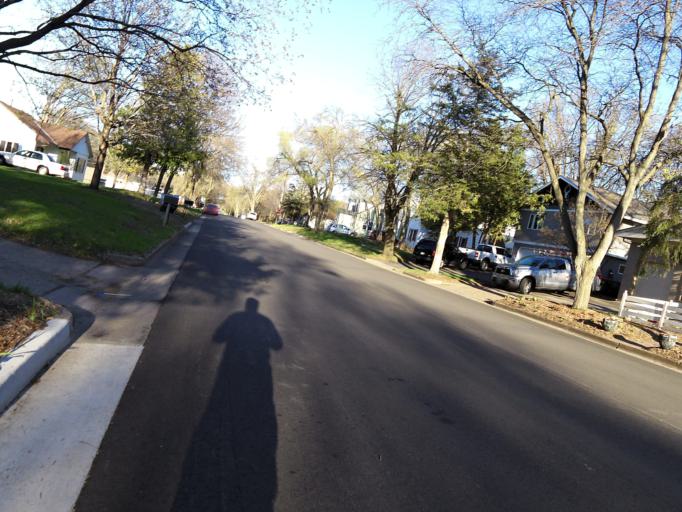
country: US
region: Wisconsin
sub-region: Saint Croix County
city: Hudson
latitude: 44.9728
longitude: -92.7505
